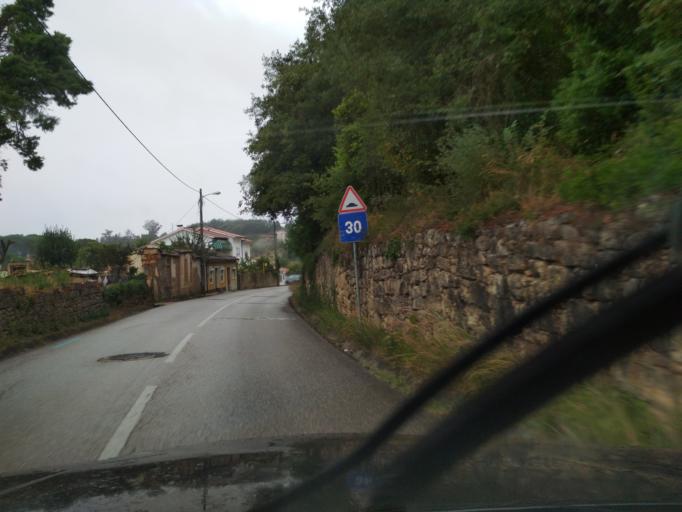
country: PT
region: Coimbra
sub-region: Coimbra
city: Coimbra
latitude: 40.1835
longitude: -8.4444
